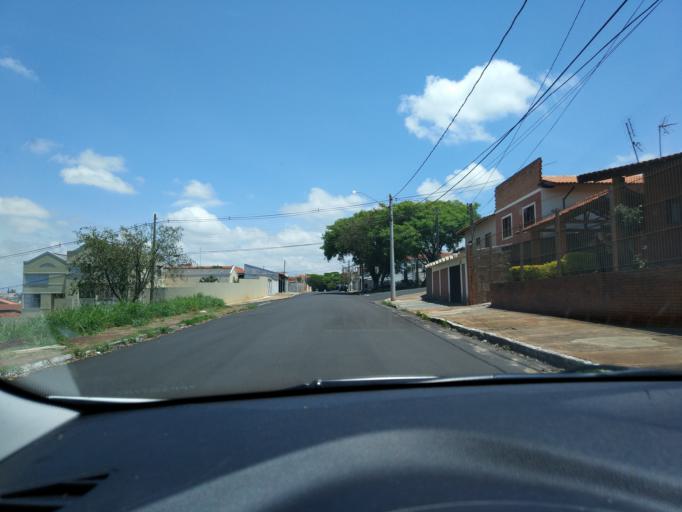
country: BR
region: Sao Paulo
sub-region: Botucatu
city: Botucatu
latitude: -22.8668
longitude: -48.4419
